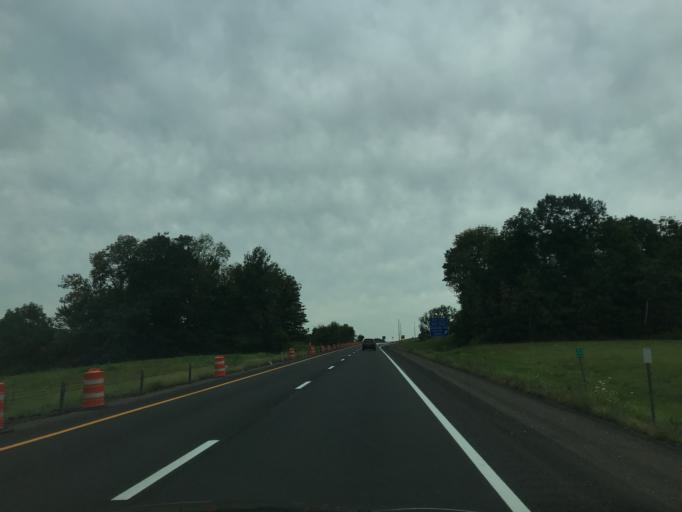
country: US
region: Pennsylvania
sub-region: Susquehanna County
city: Hallstead
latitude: 42.0169
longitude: -75.7732
